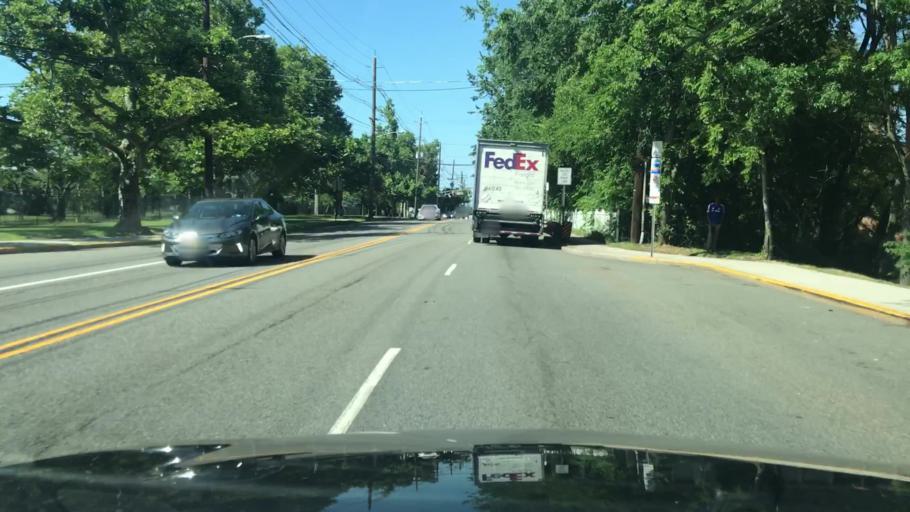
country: US
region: New Jersey
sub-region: Hudson County
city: Secaucus
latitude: 40.7843
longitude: -74.0565
